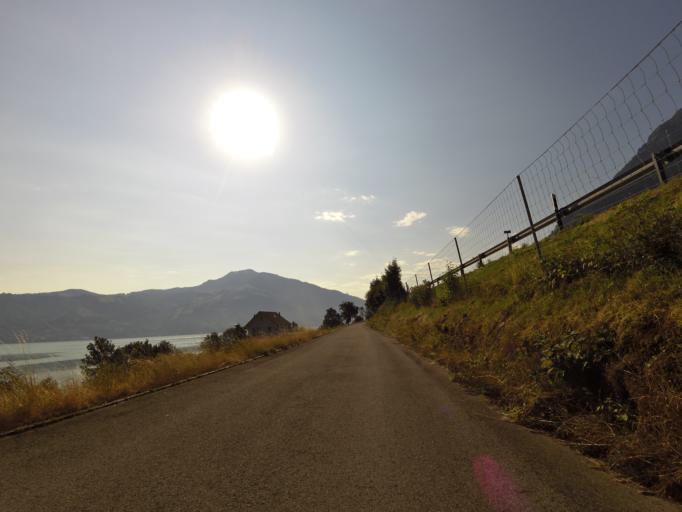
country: CH
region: Schwyz
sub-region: Bezirk Kuessnacht
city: Kussnacht
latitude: 47.0861
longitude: 8.4735
